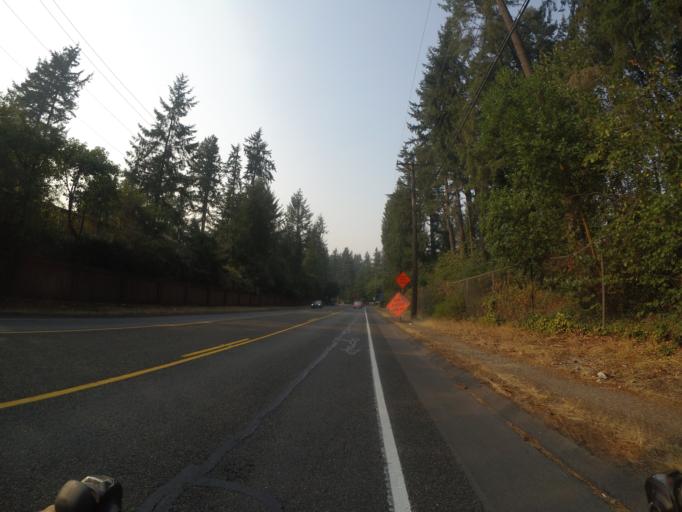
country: US
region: Washington
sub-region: Pierce County
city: Lakewood
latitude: 47.1543
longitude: -122.5238
